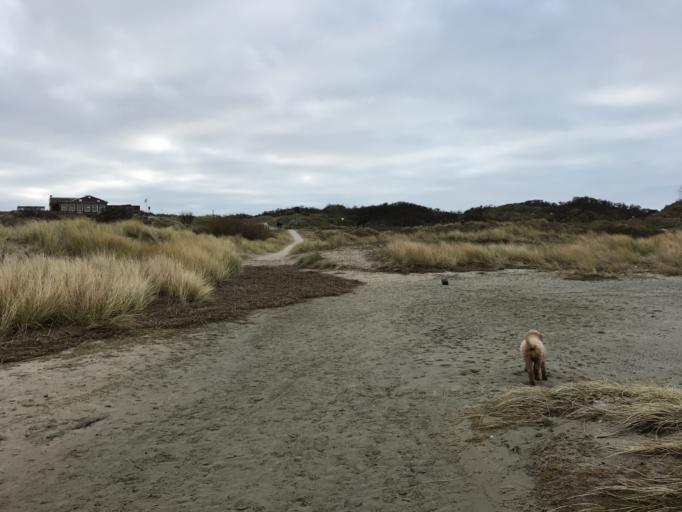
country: DE
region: Lower Saxony
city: Borkum
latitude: 53.6006
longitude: 6.6723
